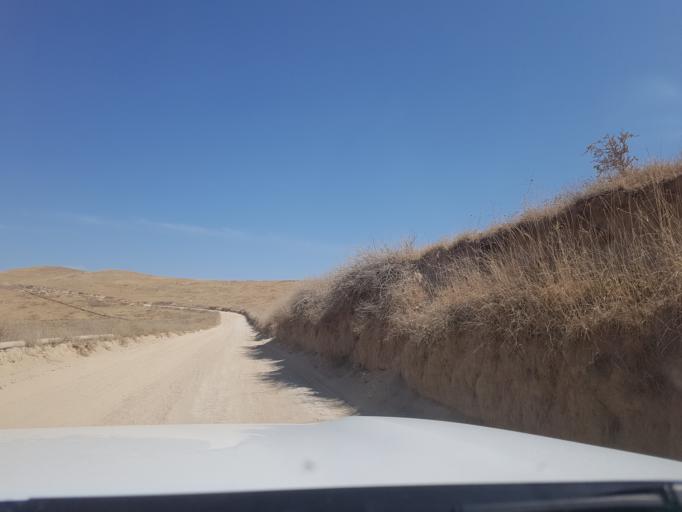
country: TM
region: Ahal
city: Baharly
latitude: 38.2696
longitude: 56.8939
